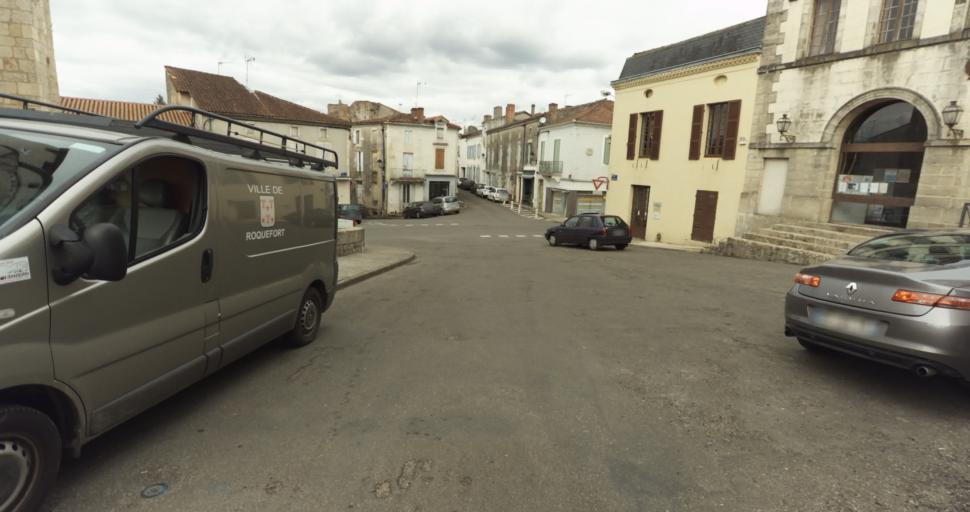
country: FR
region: Aquitaine
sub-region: Departement des Landes
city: Roquefort
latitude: 44.0342
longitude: -0.3230
